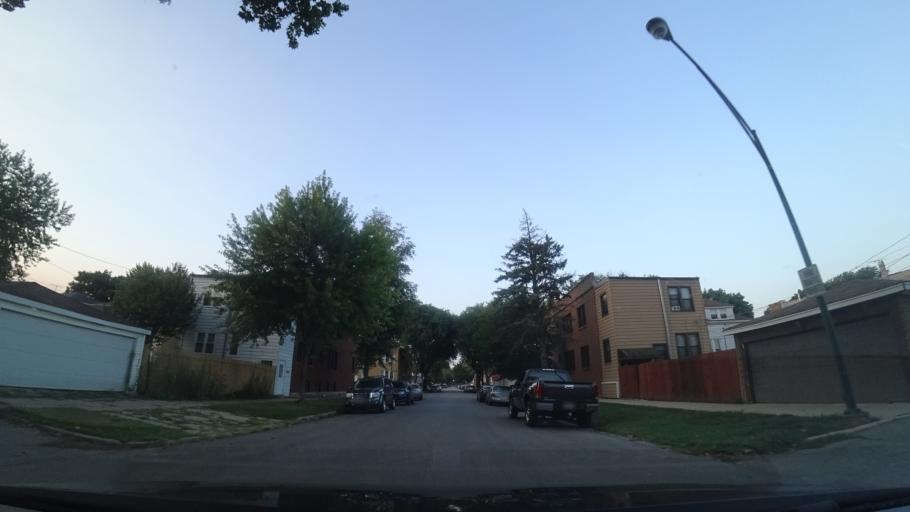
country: US
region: Illinois
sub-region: Cook County
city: Harwood Heights
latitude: 41.9665
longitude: -87.7699
